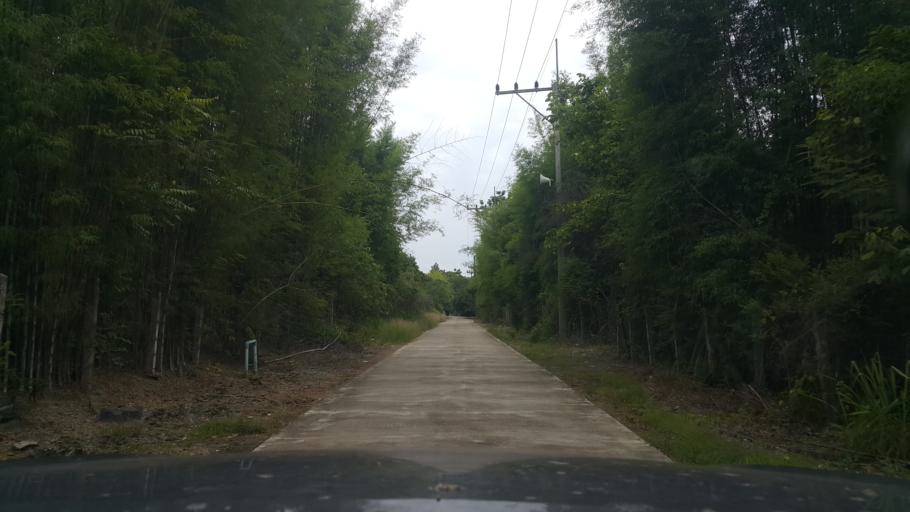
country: TH
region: Chiang Mai
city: San Pa Tong
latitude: 18.6463
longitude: 98.8430
